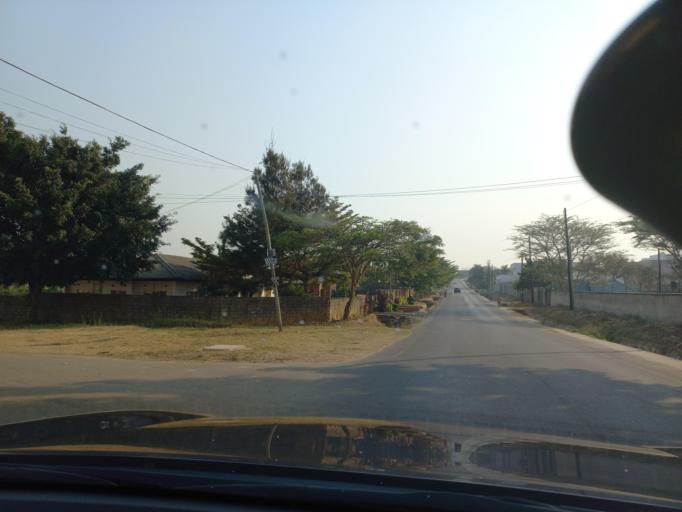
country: ZM
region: Lusaka
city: Lusaka
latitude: -15.4239
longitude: 28.3626
